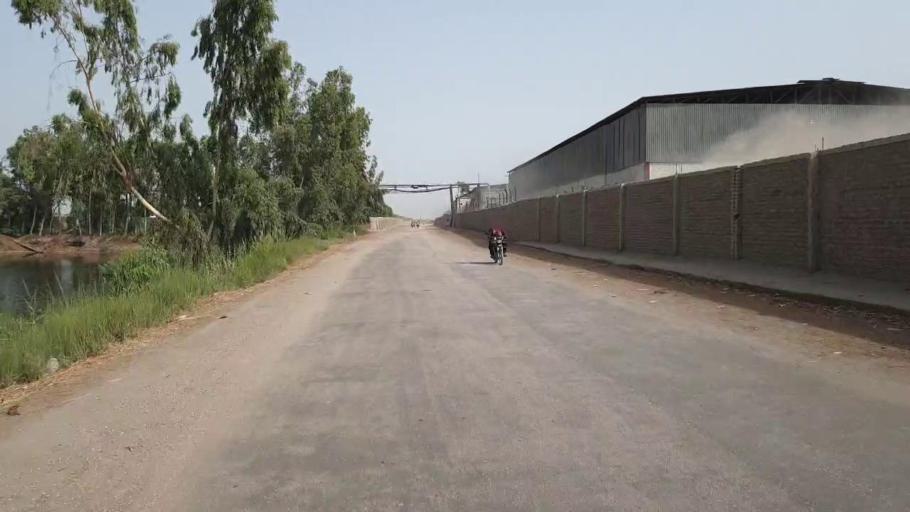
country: PK
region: Sindh
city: Daulatpur
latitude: 26.5586
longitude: 67.9886
